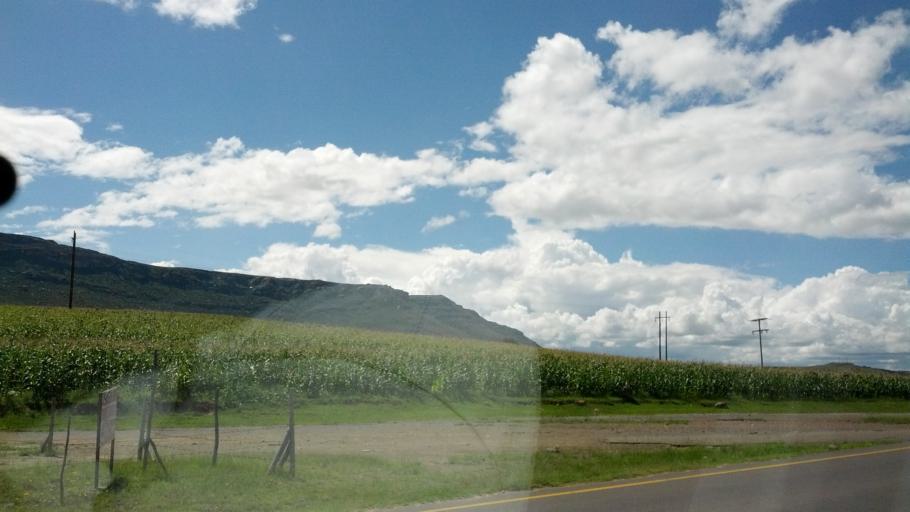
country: LS
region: Maseru
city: Nako
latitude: -29.6326
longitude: 27.4814
